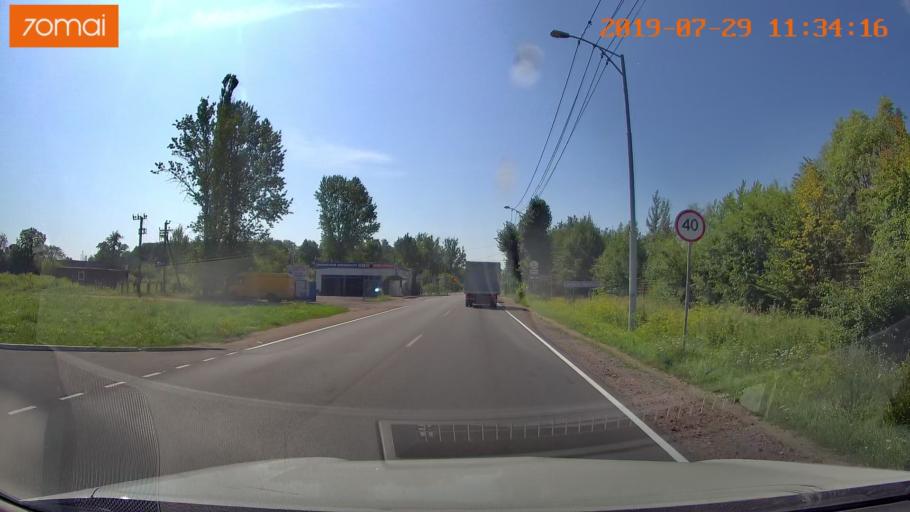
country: RU
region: Kaliningrad
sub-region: Gorod Kaliningrad
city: Kaliningrad
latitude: 54.6575
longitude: 20.5419
